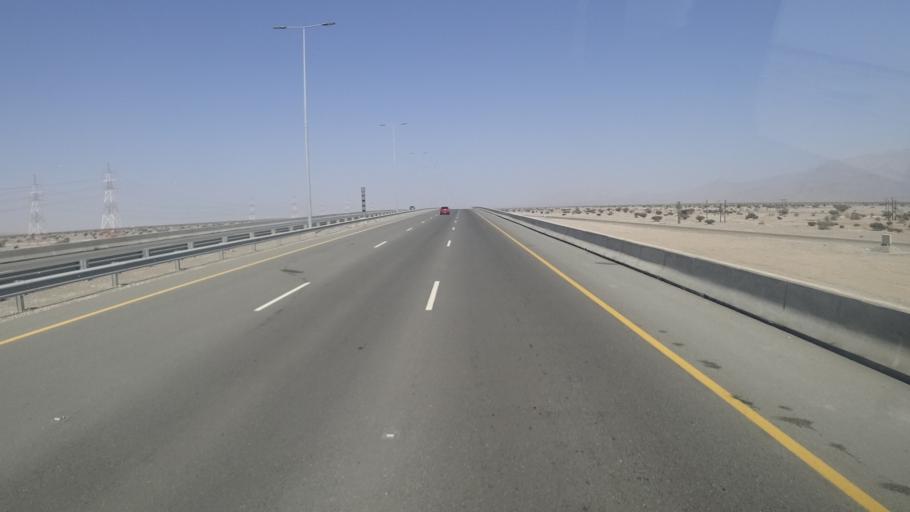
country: OM
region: Ash Sharqiyah
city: Badiyah
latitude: 22.3187
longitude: 59.1366
